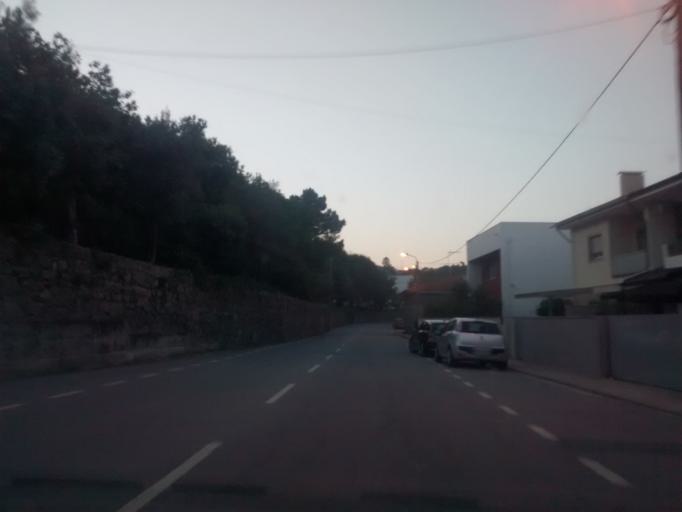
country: PT
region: Braga
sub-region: Braga
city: Adaufe
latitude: 41.5646
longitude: -8.3927
